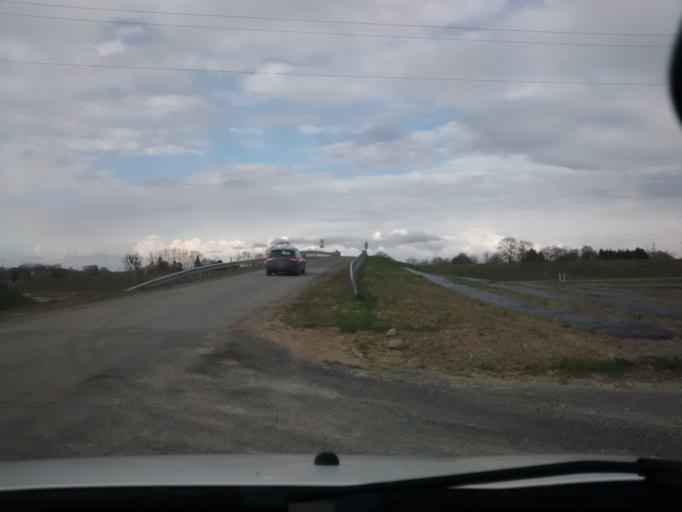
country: FR
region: Brittany
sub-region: Departement d'Ille-et-Vilaine
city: Cesson-Sevigne
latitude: 48.1035
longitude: -1.5796
